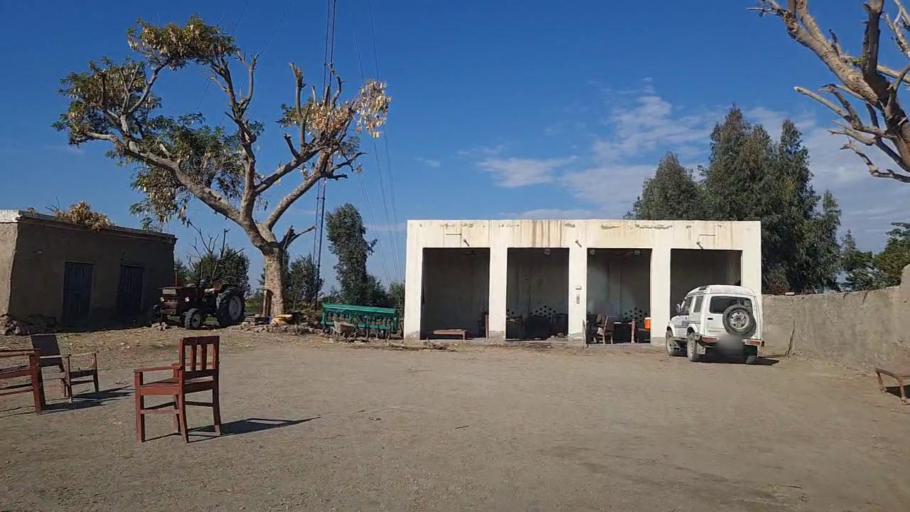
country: PK
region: Sindh
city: Khadro
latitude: 26.2716
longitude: 68.8146
